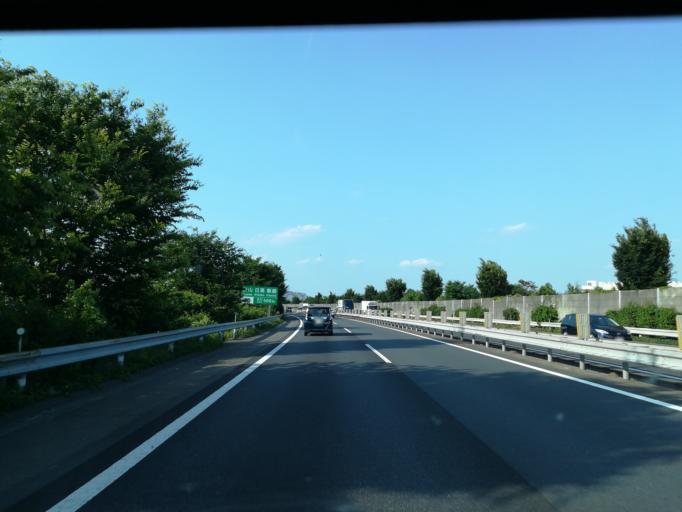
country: JP
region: Saitama
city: Sayama
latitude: 35.8605
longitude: 139.3759
